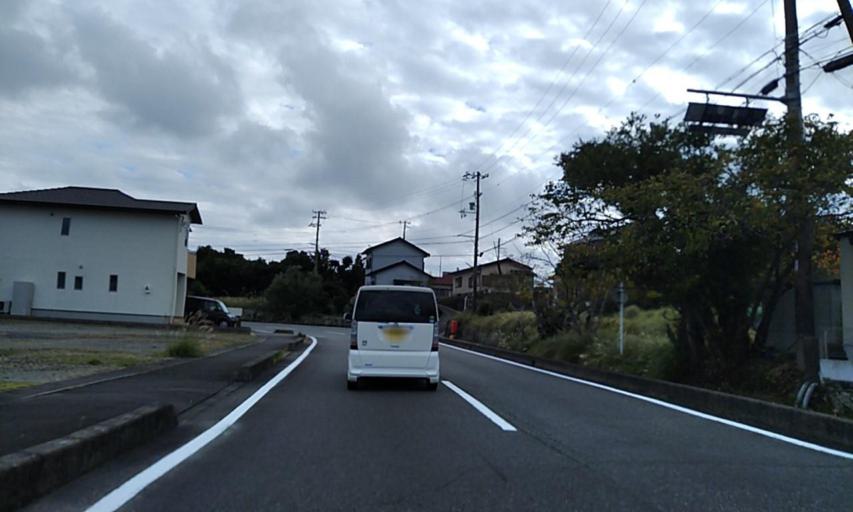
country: JP
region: Wakayama
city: Shingu
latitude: 33.5862
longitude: 135.9477
